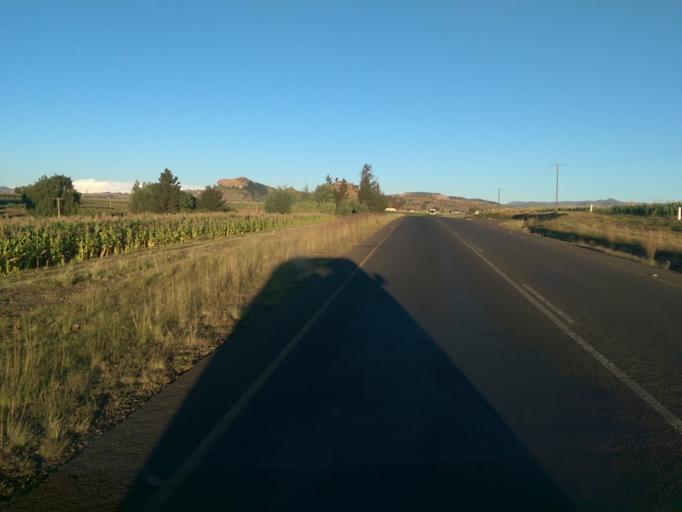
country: LS
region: Maseru
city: Maseru
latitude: -29.4081
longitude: 27.6013
